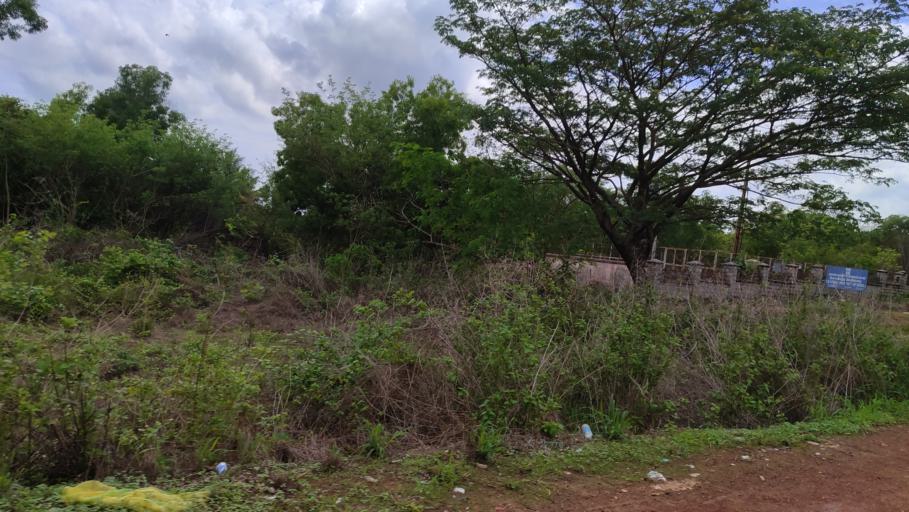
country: IN
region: Kerala
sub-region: Kasaragod District
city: Kannangad
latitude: 12.3921
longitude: 75.1007
